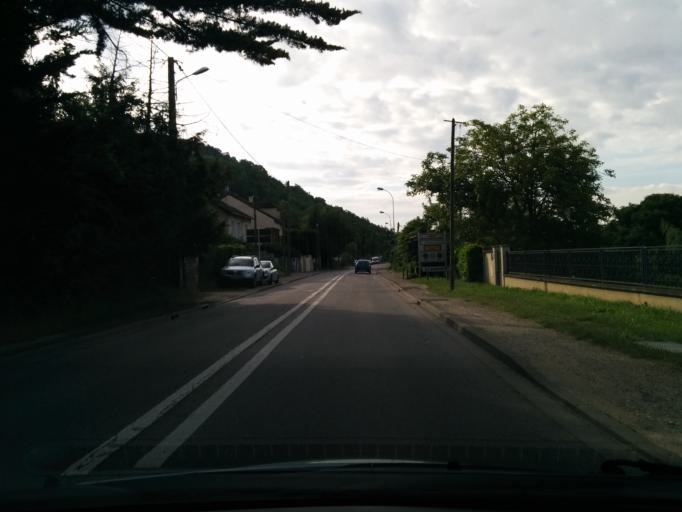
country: FR
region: Ile-de-France
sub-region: Departement des Yvelines
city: Follainville-Dennemont
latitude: 49.0095
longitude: 1.7087
